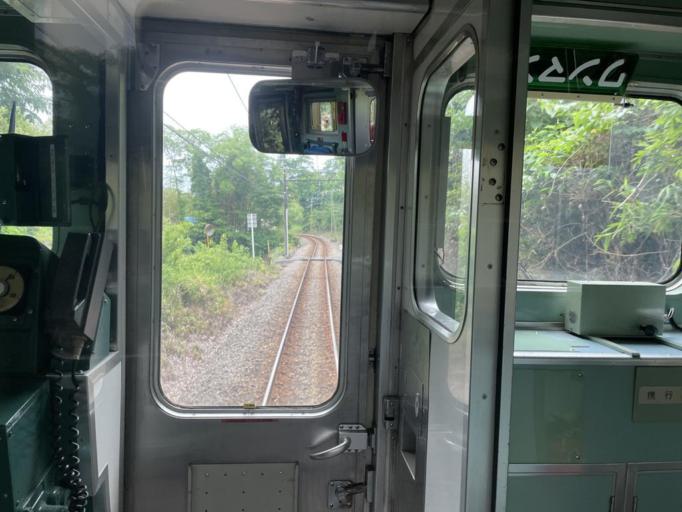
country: JP
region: Gunma
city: Takasaki
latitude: 36.2827
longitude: 139.0325
